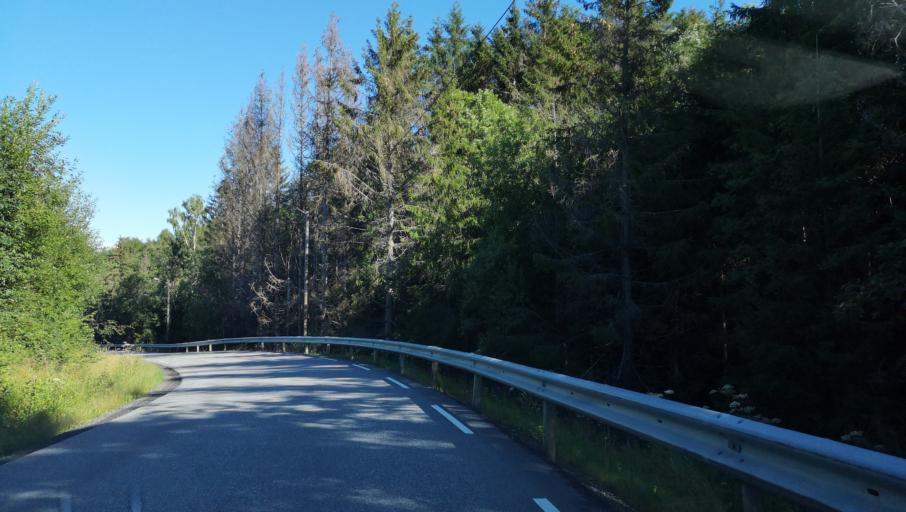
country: NO
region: Ostfold
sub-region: Hobol
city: Tomter
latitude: 59.6548
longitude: 11.0085
